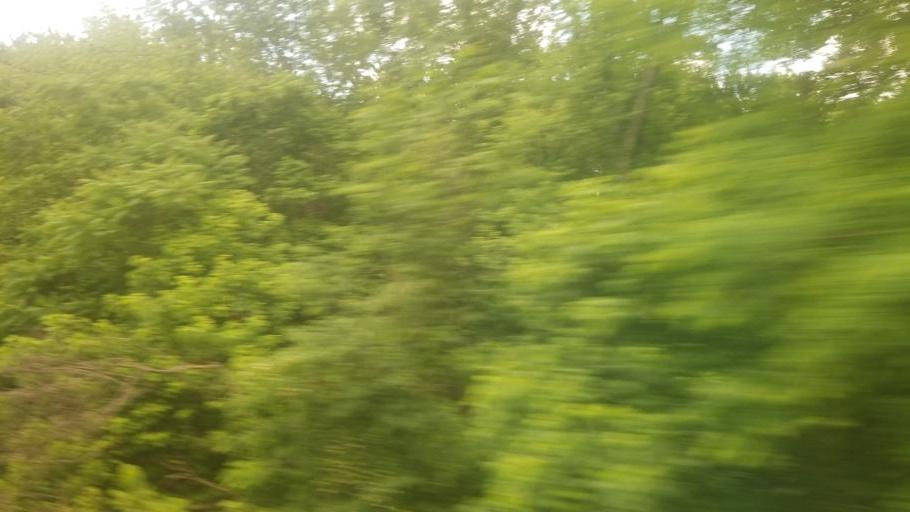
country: US
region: Maryland
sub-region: Frederick County
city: Brunswick
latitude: 39.3053
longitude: -77.5960
